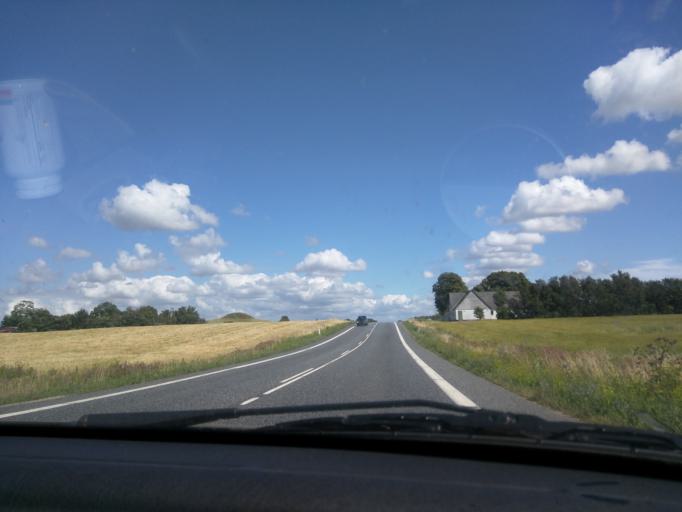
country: DK
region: Zealand
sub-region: Kalundborg Kommune
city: Kalundborg
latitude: 55.6763
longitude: 11.1603
